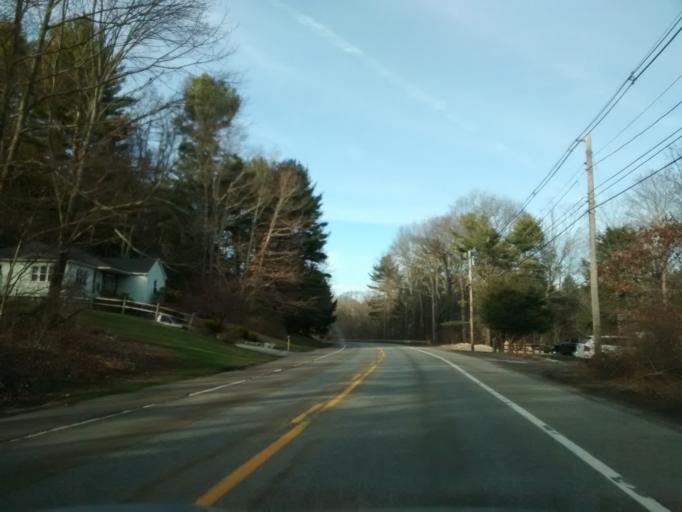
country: US
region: Massachusetts
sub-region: Worcester County
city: Charlton
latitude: 42.1330
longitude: -72.0020
